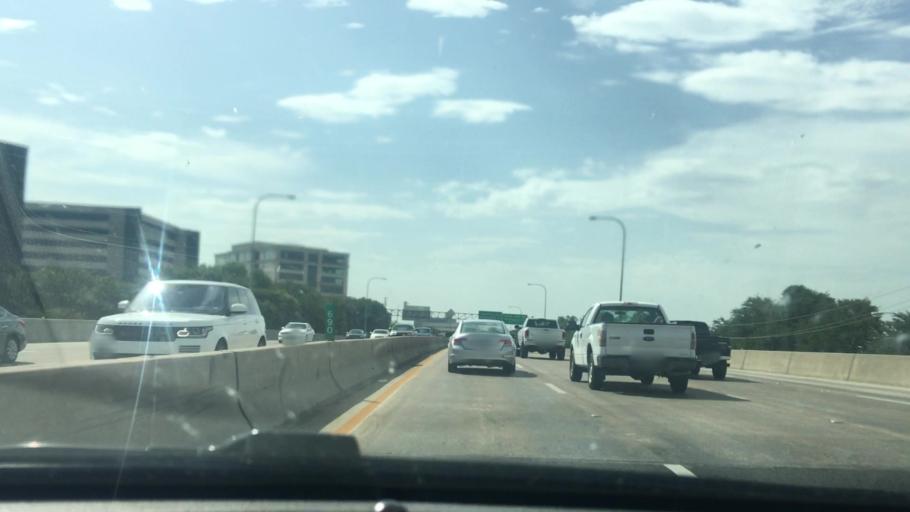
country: US
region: Texas
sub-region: Dallas County
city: Addison
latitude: 32.9750
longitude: -96.8233
